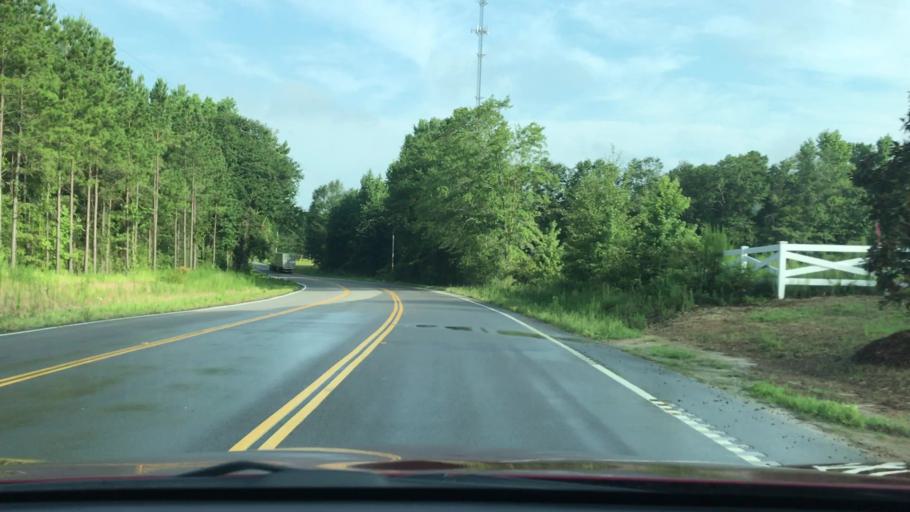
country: US
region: South Carolina
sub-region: Bamberg County
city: Denmark
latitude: 33.5386
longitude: -81.1358
